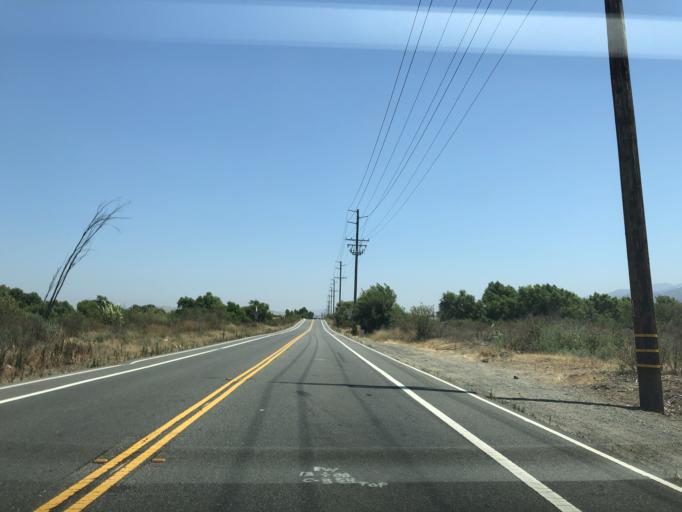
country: US
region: California
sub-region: Riverside County
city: Corona
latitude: 33.9032
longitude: -117.5985
